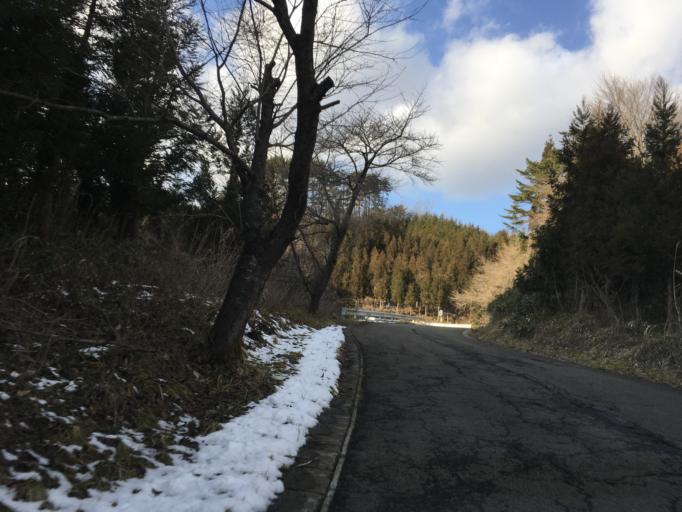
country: JP
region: Miyagi
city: Furukawa
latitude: 38.8175
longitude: 140.8328
